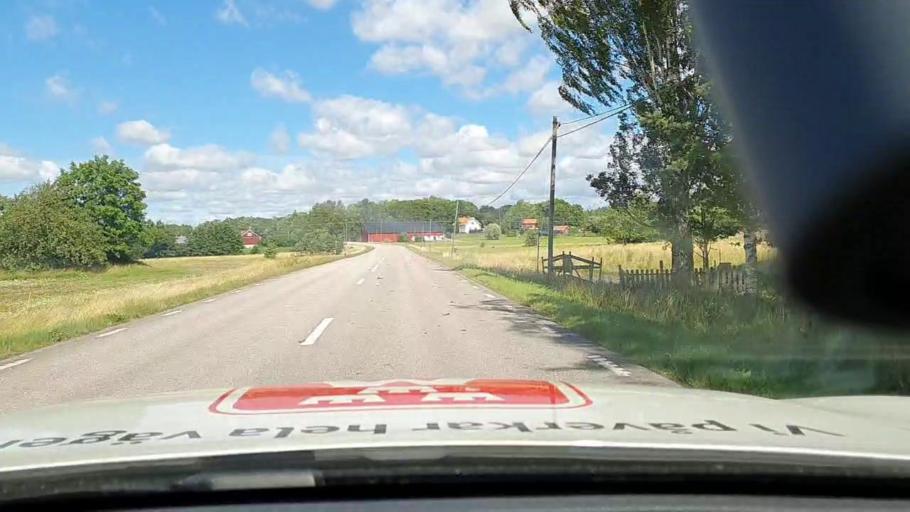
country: SE
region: Vaestra Goetaland
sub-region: Skovde Kommun
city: Stopen
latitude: 58.5147
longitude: 13.9757
